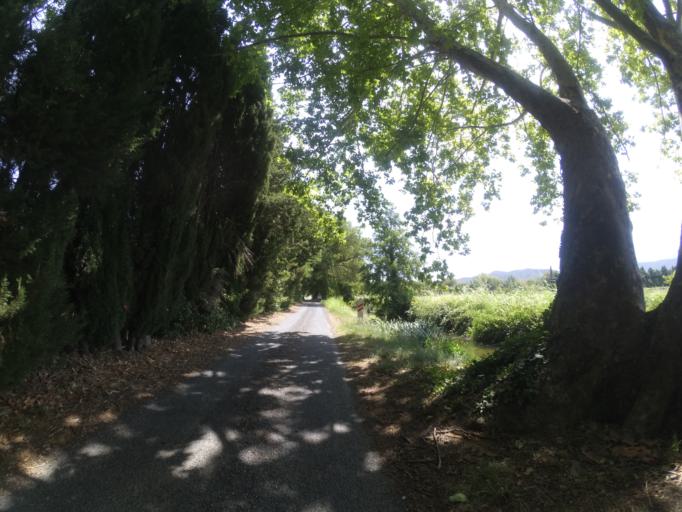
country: FR
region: Languedoc-Roussillon
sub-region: Departement des Pyrenees-Orientales
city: Ille-sur-Tet
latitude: 42.6794
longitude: 2.6456
